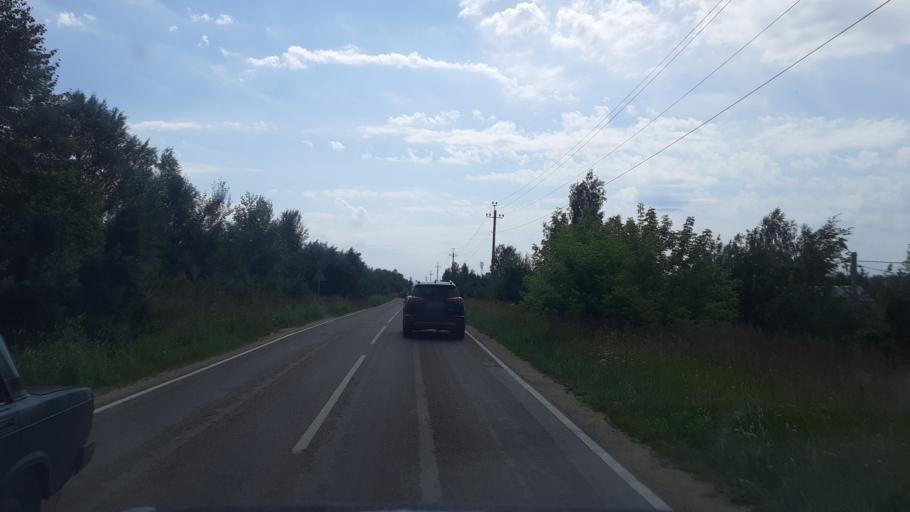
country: RU
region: Moskovskaya
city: Chupryakovo
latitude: 55.5648
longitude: 36.5692
